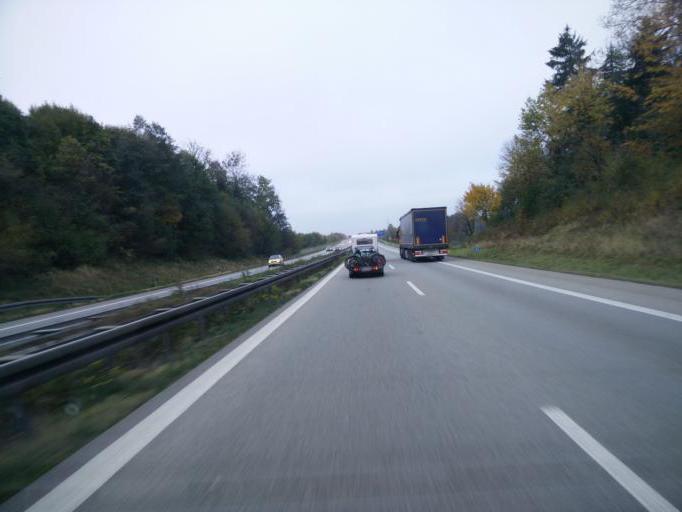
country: DE
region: Bavaria
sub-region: Swabia
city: Stetten
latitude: 48.0321
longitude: 10.4517
